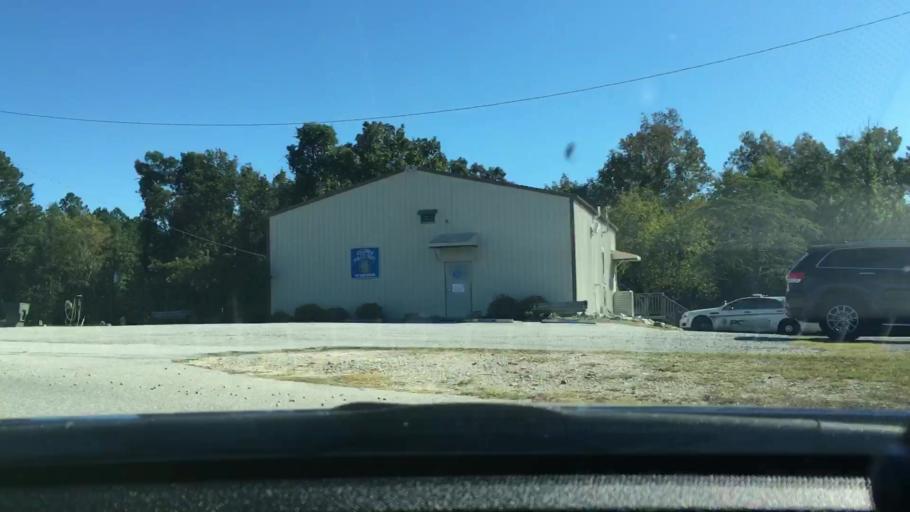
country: US
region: South Carolina
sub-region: Lexington County
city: Irmo
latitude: 34.0861
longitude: -81.1491
